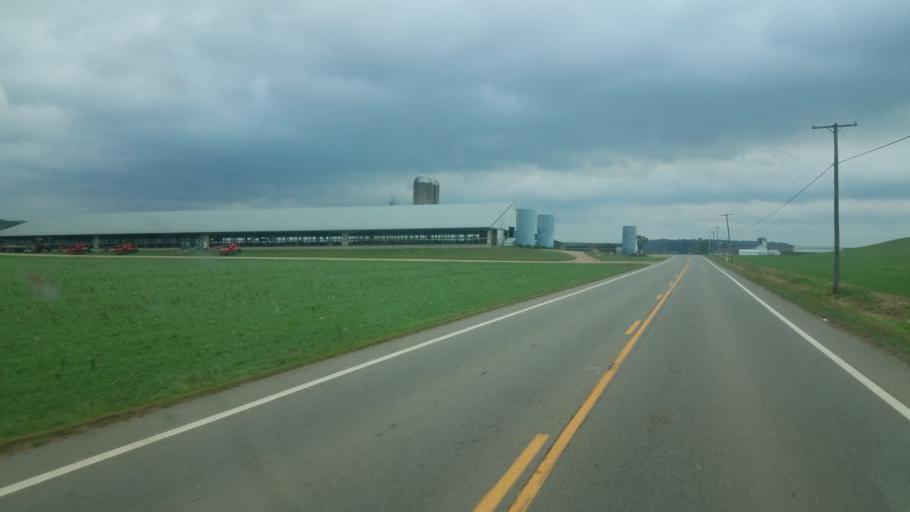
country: US
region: Ohio
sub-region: Ashland County
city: Loudonville
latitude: 40.6530
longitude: -82.2879
